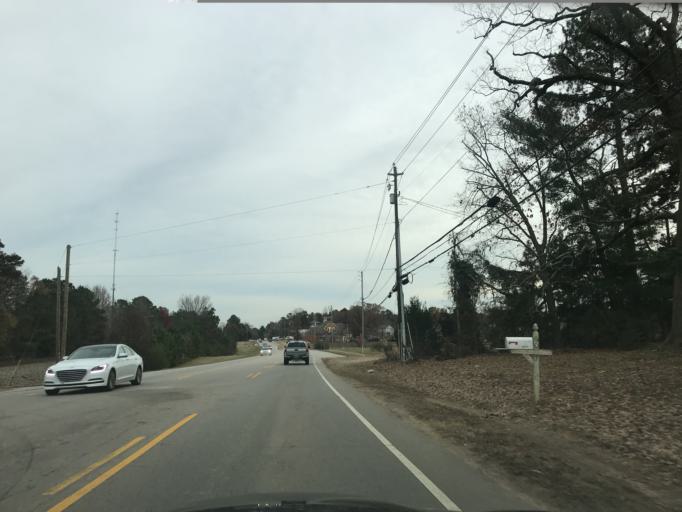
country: US
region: North Carolina
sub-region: Wake County
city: Cary
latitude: 35.7870
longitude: -78.7330
